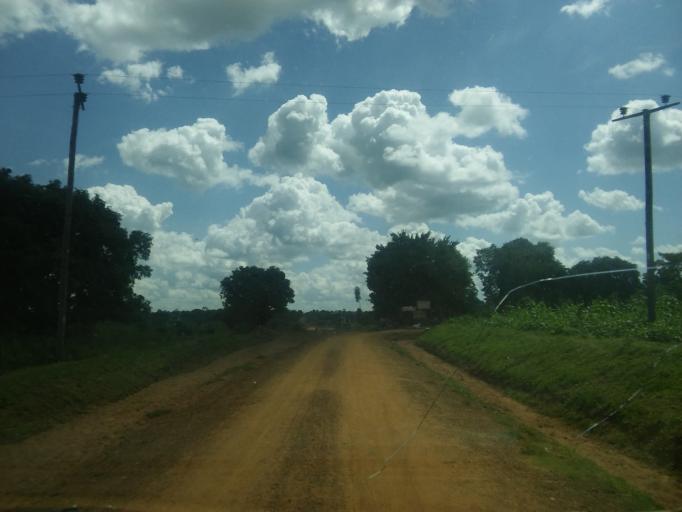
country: UG
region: Eastern Region
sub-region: Kibuku District
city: Kibuku
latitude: 1.1494
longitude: 33.8220
